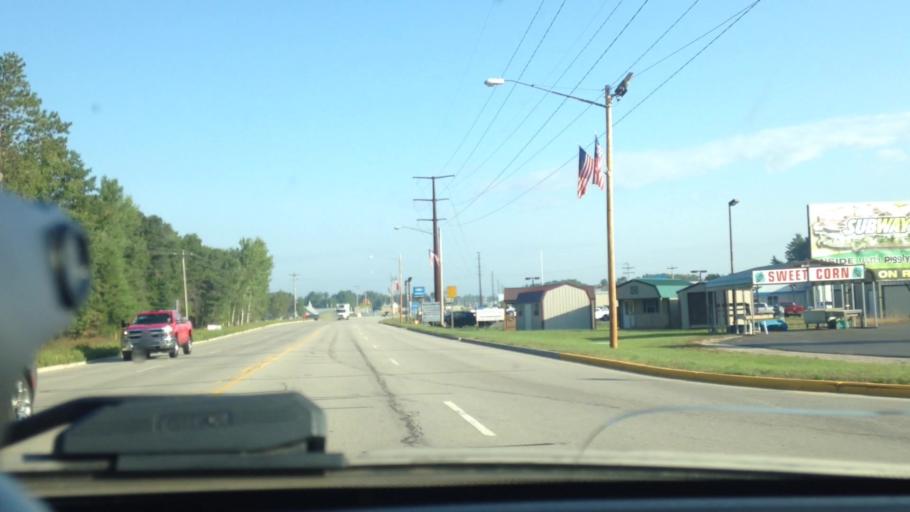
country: US
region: Wisconsin
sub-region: Marinette County
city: Peshtigo
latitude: 45.2179
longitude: -87.9967
